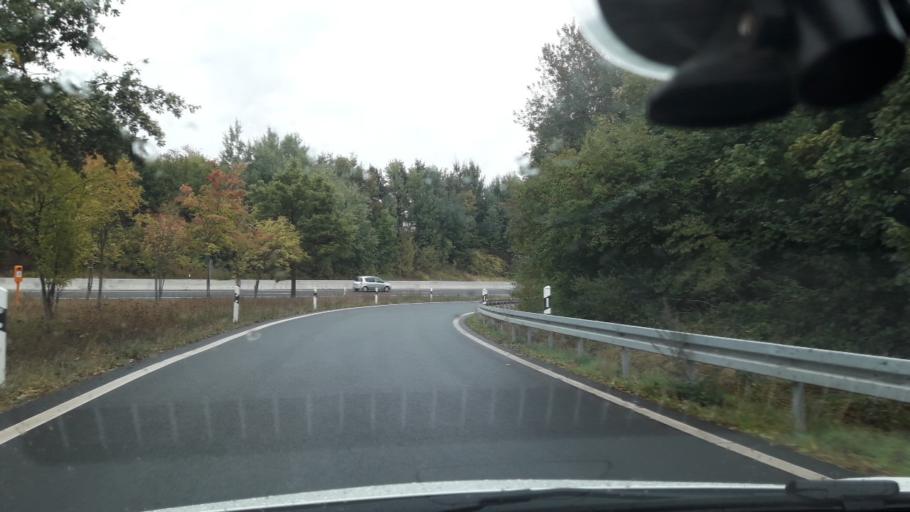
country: DE
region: Lower Saxony
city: Schladen
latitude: 52.0242
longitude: 10.5224
